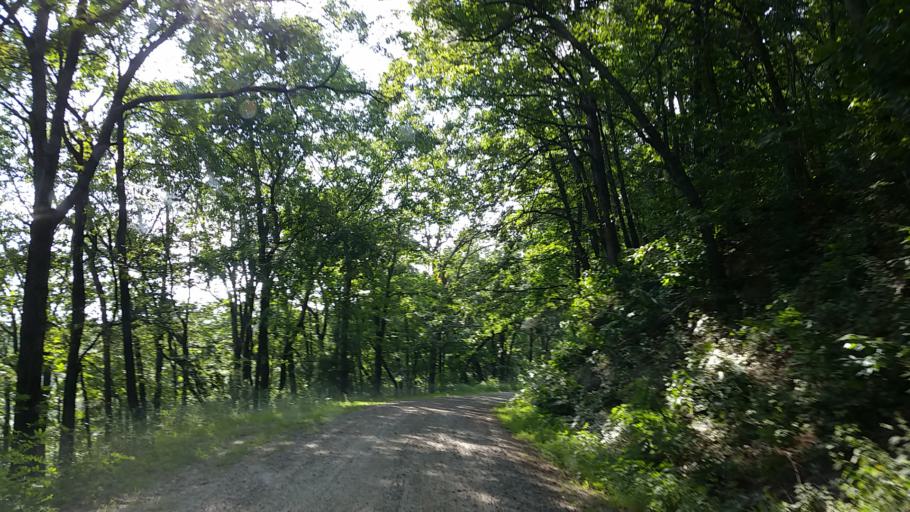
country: US
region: Georgia
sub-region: Lumpkin County
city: Dahlonega
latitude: 34.6381
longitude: -84.0355
